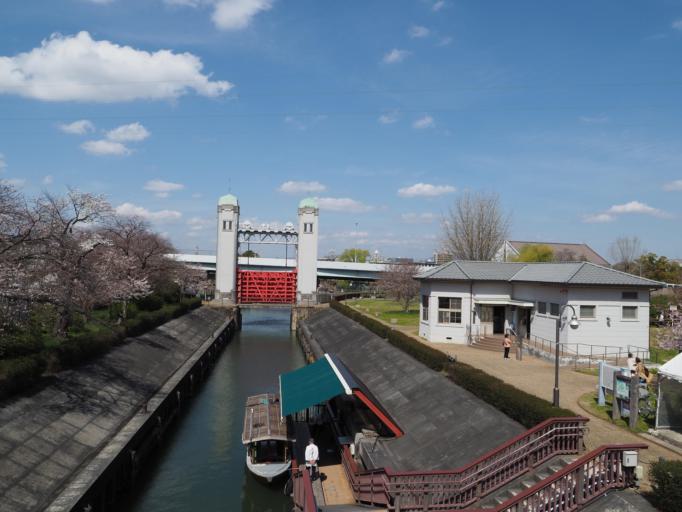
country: JP
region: Kyoto
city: Uji
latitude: 34.9231
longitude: 135.7561
